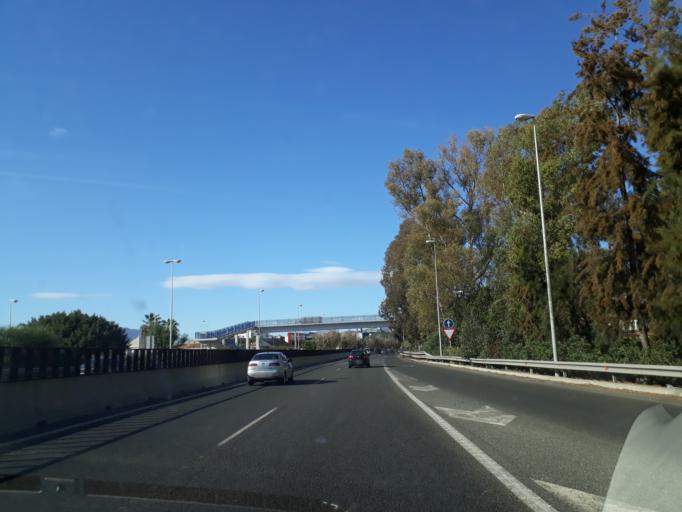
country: ES
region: Andalusia
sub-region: Provincia de Malaga
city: Fuengirola
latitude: 36.5325
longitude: -4.6312
